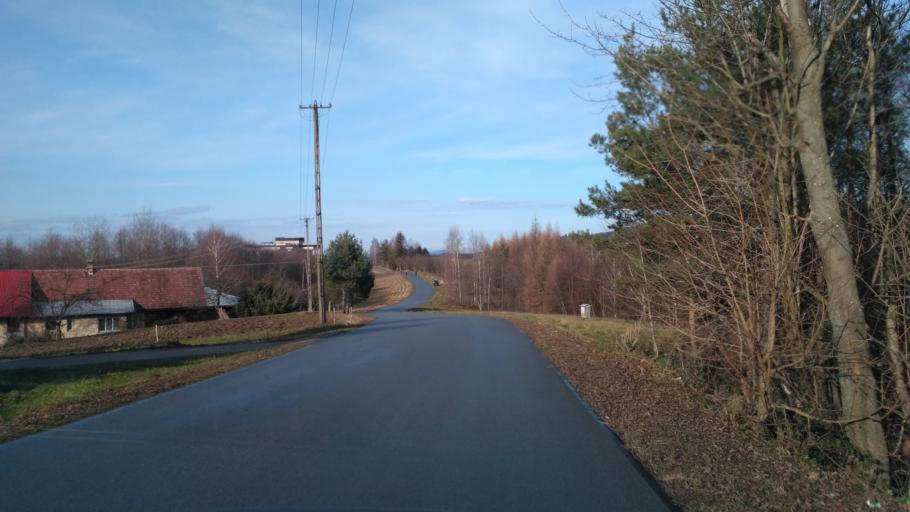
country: PL
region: Subcarpathian Voivodeship
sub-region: Powiat krosnienski
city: Korczyna
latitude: 49.7304
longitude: 21.7888
